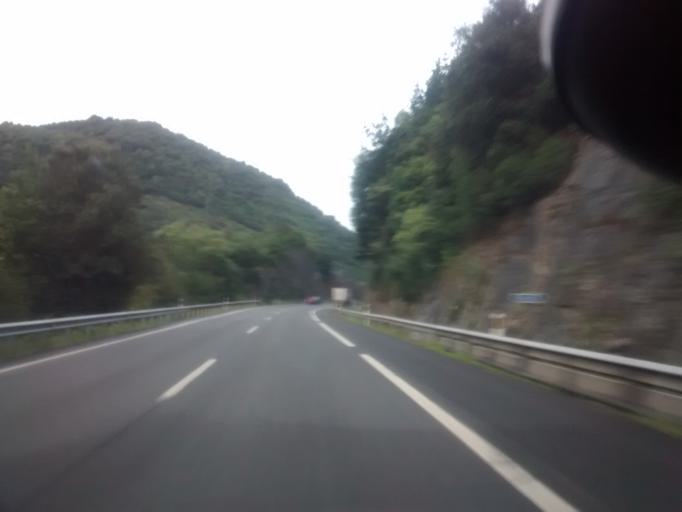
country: ES
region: Basque Country
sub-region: Provincia de Guipuzcoa
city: Mendaro
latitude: 43.2610
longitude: -2.3803
